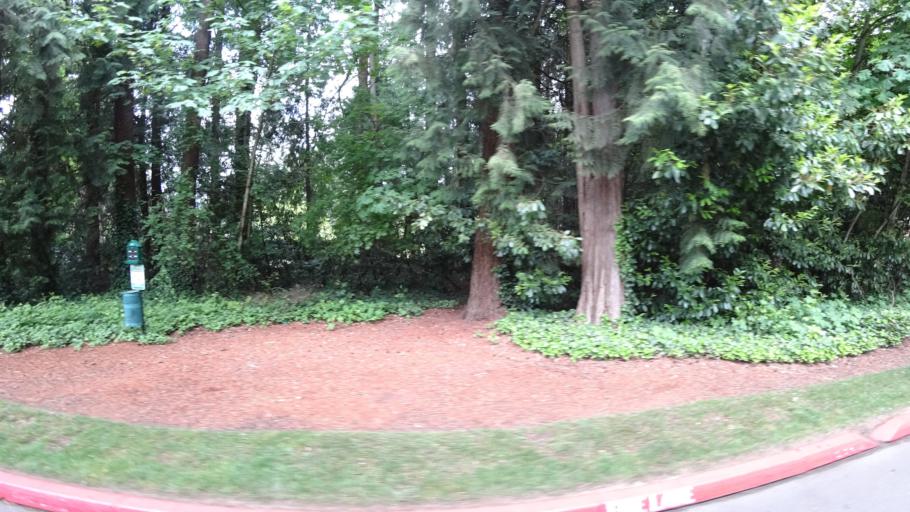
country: US
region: Oregon
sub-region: Washington County
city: Garden Home-Whitford
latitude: 45.4691
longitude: -122.7537
